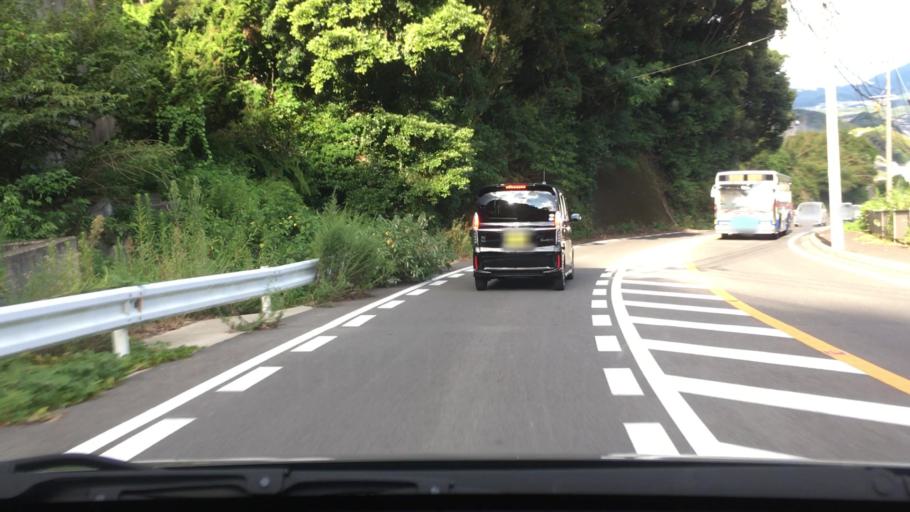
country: JP
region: Nagasaki
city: Togitsu
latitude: 32.8109
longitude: 129.8178
